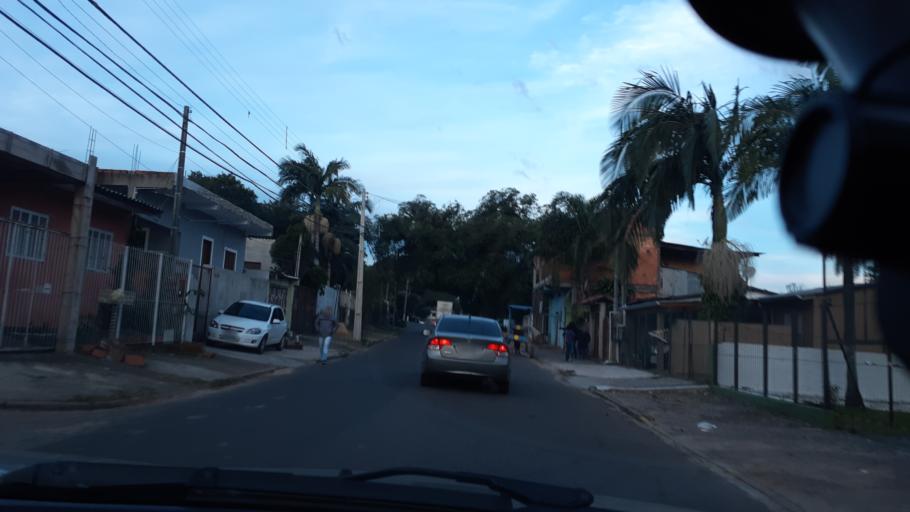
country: BR
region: Rio Grande do Sul
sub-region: Sapucaia Do Sul
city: Sapucaia
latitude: -29.8427
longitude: -51.1520
